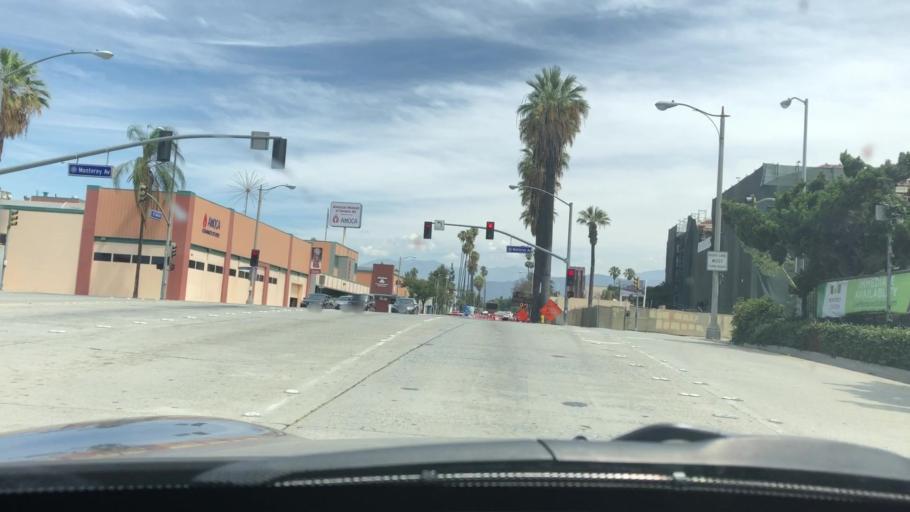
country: US
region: California
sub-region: Los Angeles County
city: Pomona
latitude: 34.0602
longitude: -117.7502
